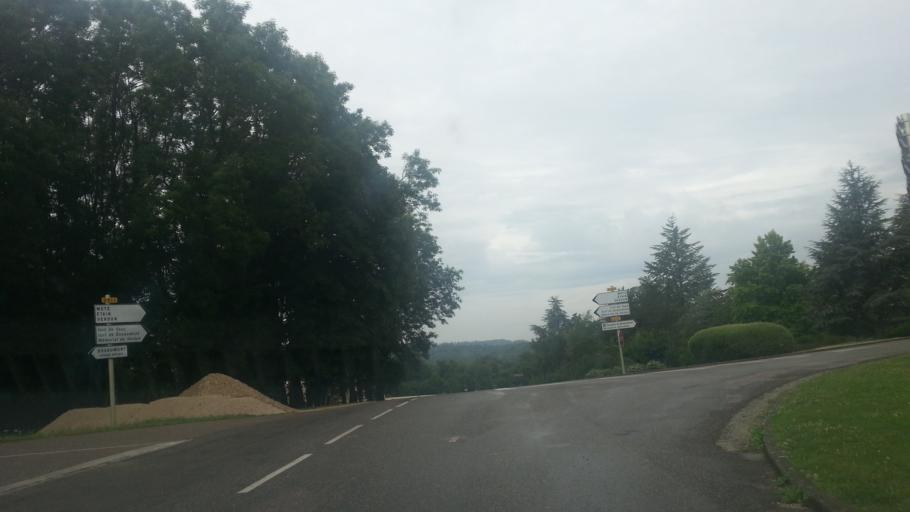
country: FR
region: Lorraine
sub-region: Departement de la Meuse
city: Verdun
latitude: 49.2100
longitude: 5.4277
